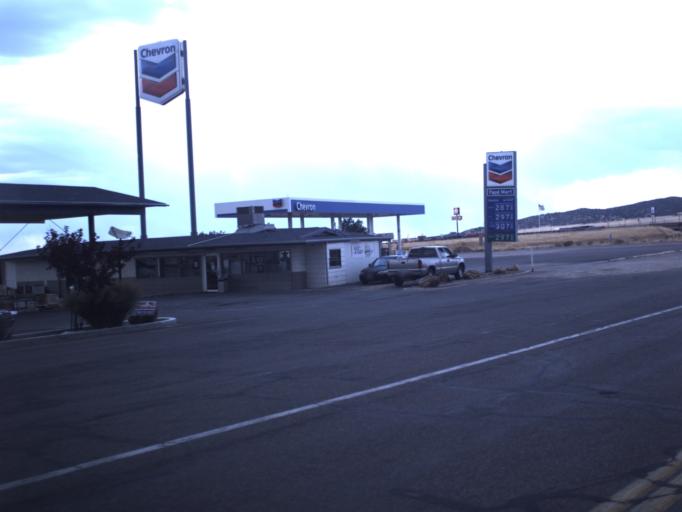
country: US
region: Utah
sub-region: Millard County
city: Fillmore
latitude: 38.9886
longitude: -112.3233
